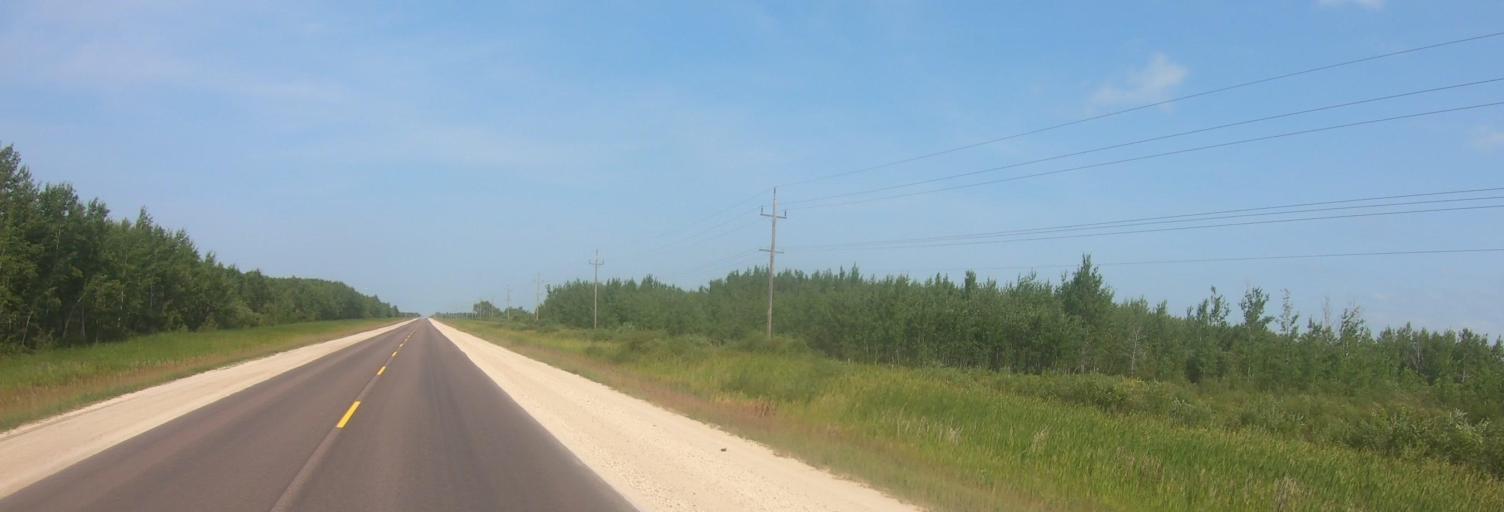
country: CA
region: Manitoba
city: La Broquerie
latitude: 49.2695
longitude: -96.4799
